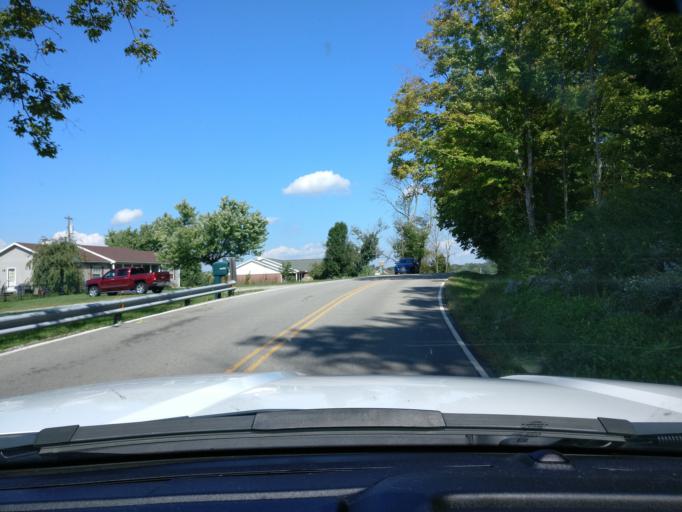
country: US
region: Ohio
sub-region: Warren County
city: Waynesville
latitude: 39.4960
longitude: -84.0027
